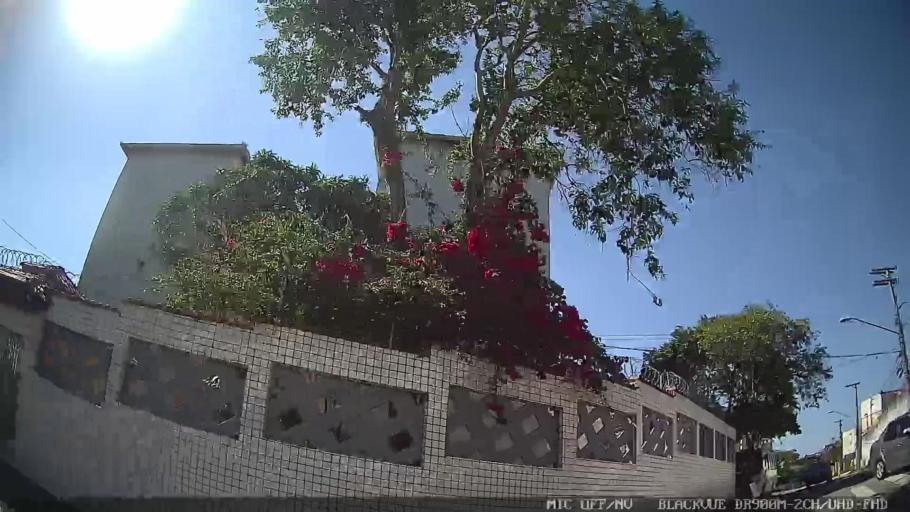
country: BR
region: Sao Paulo
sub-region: Sao Caetano Do Sul
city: Sao Caetano do Sul
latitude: -23.5515
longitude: -46.4910
